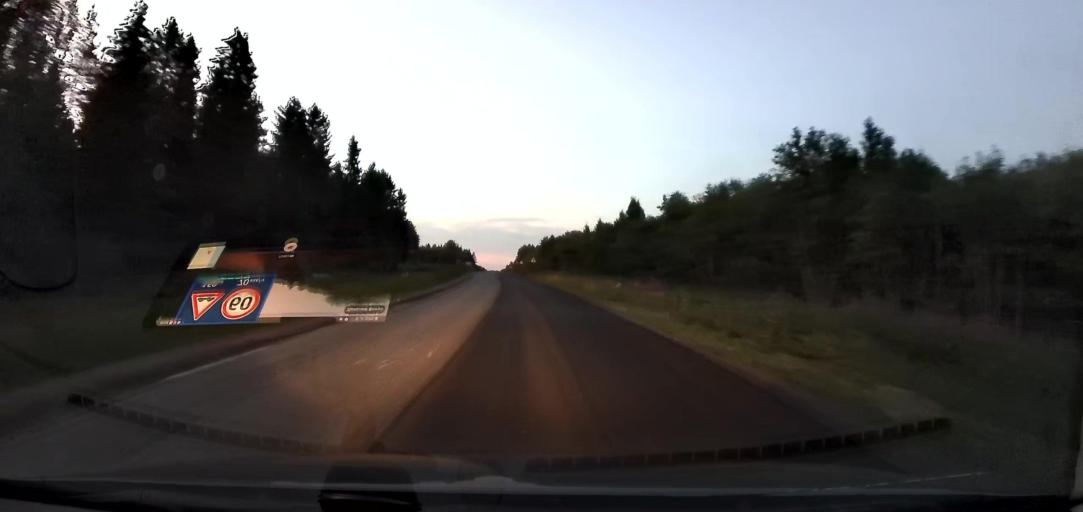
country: RU
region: Arkhangelskaya
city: Kholmogory
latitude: 64.3285
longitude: 41.4211
